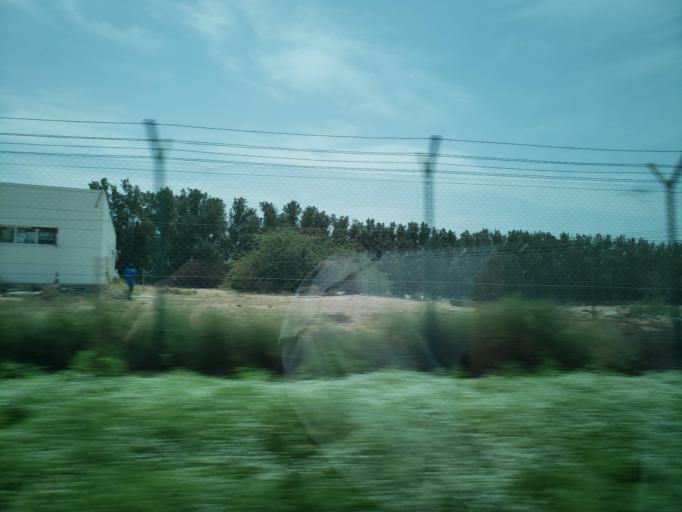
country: AE
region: Ash Shariqah
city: Sharjah
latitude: 25.3216
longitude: 55.5077
